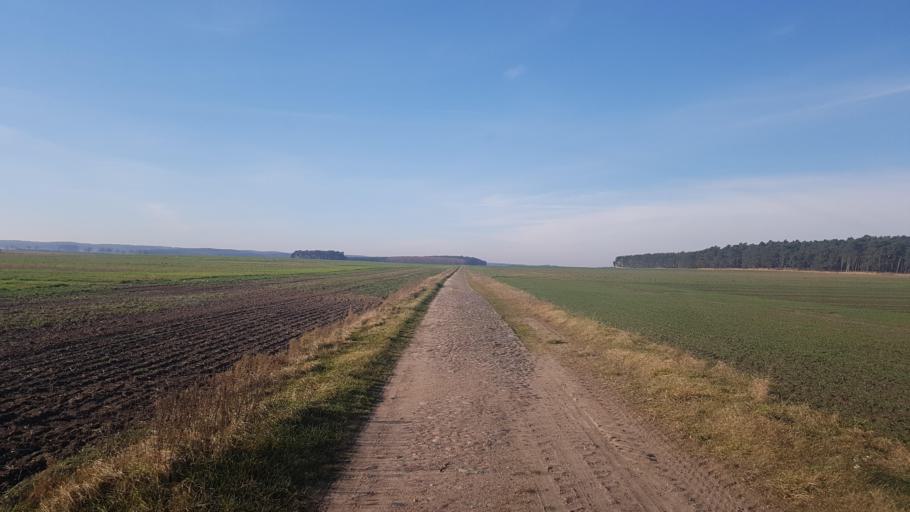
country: DE
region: Brandenburg
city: Niemegk
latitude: 52.1187
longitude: 12.6714
